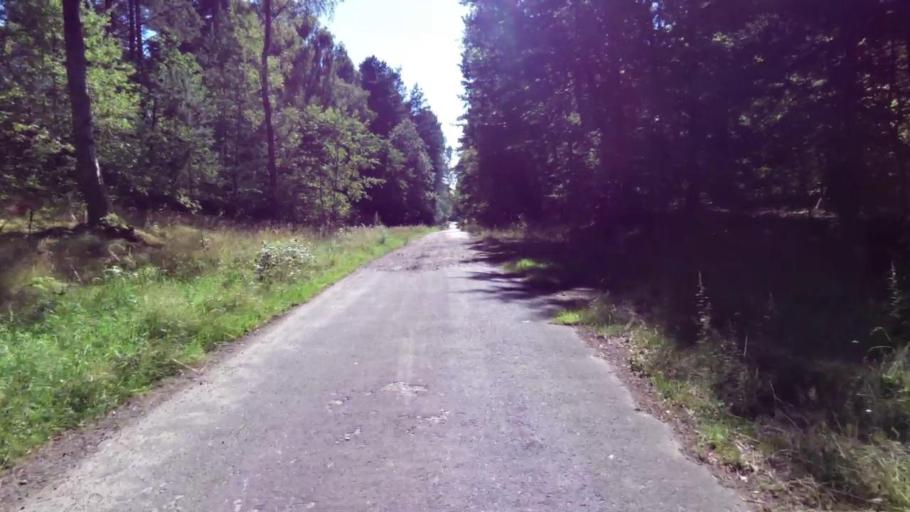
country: PL
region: West Pomeranian Voivodeship
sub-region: Powiat szczecinecki
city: Borne Sulinowo
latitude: 53.5996
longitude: 16.6029
